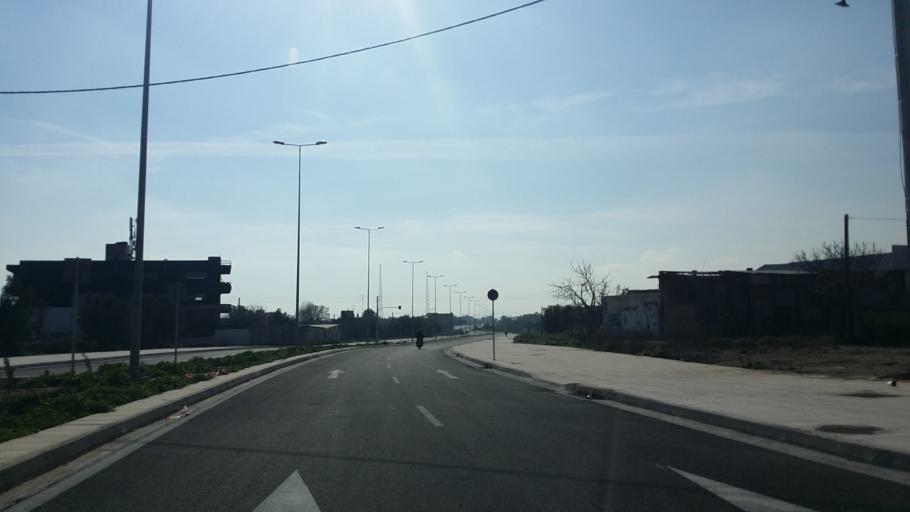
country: GR
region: Attica
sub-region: Nomarchia Athinas
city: Kamateron
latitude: 38.0501
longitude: 23.7156
